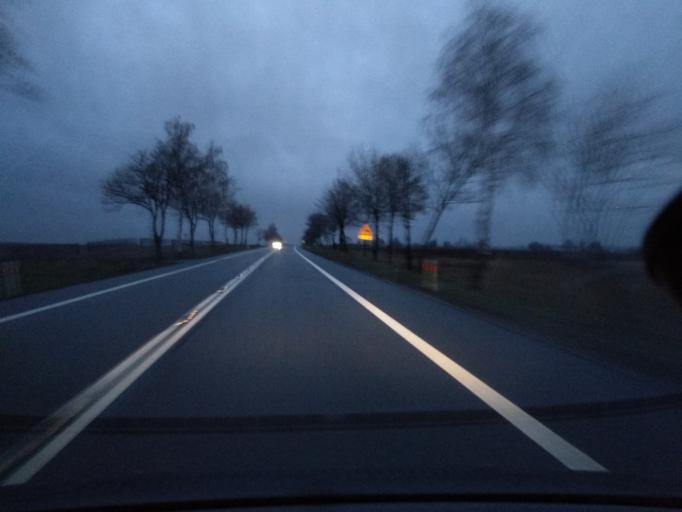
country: PL
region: Lower Silesian Voivodeship
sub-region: Powiat sredzki
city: Miekinia
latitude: 51.1608
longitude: 16.7035
